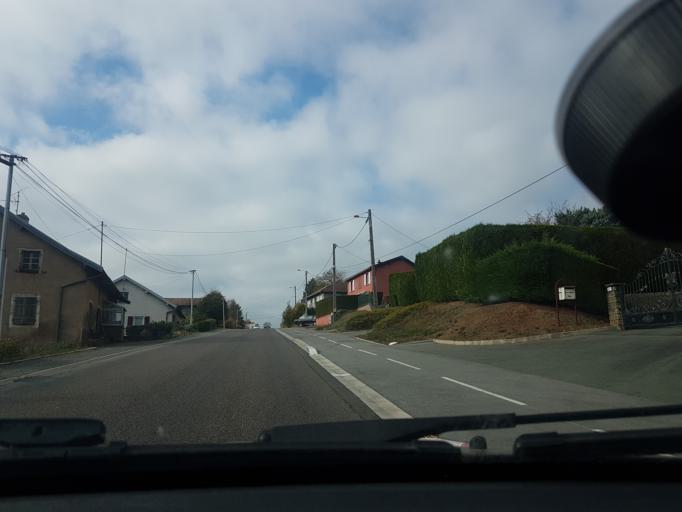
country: FR
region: Franche-Comte
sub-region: Departement de la Haute-Saone
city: Chalonvillars
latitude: 47.6441
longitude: 6.7860
